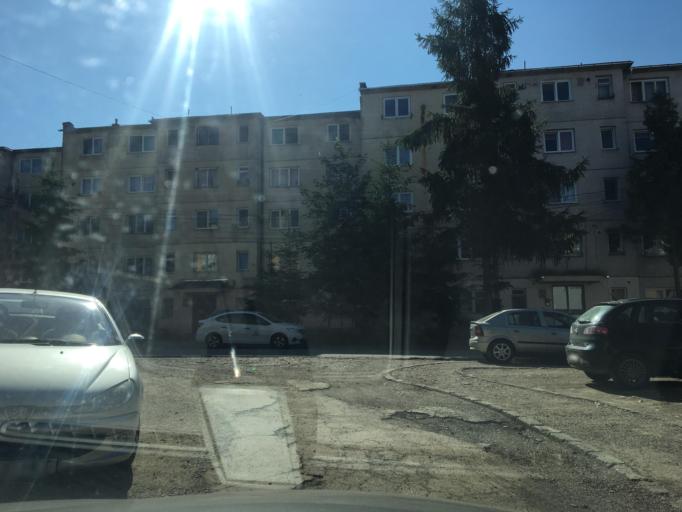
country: RO
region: Harghita
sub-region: Municipiul Gheorgheni
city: Gheorgheni
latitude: 46.7208
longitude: 25.5913
